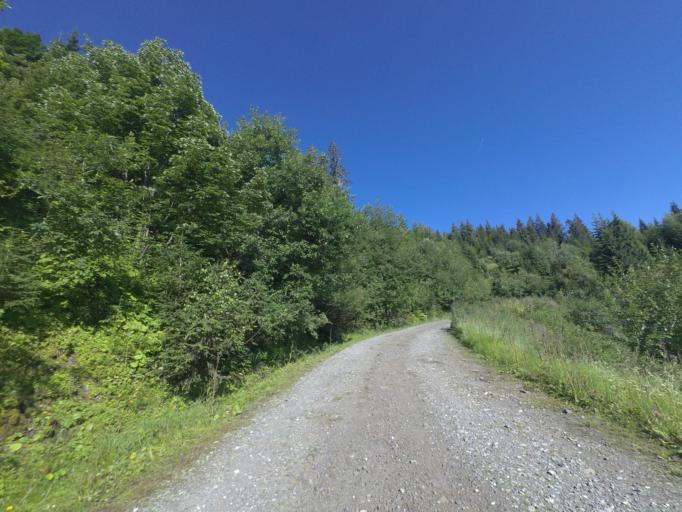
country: AT
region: Salzburg
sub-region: Politischer Bezirk Sankt Johann im Pongau
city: Sankt Veit im Pongau
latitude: 47.3467
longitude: 13.1486
